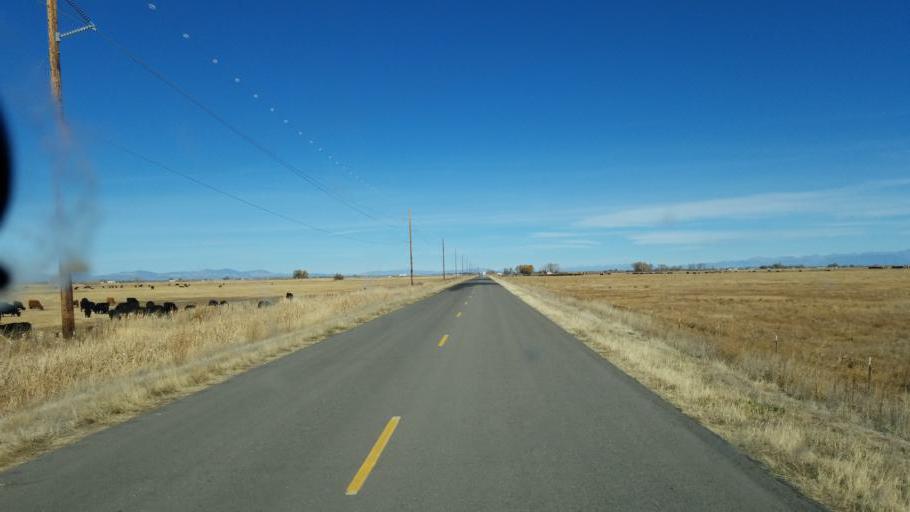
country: US
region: Colorado
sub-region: Rio Grande County
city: Monte Vista
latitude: 37.5122
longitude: -106.0941
